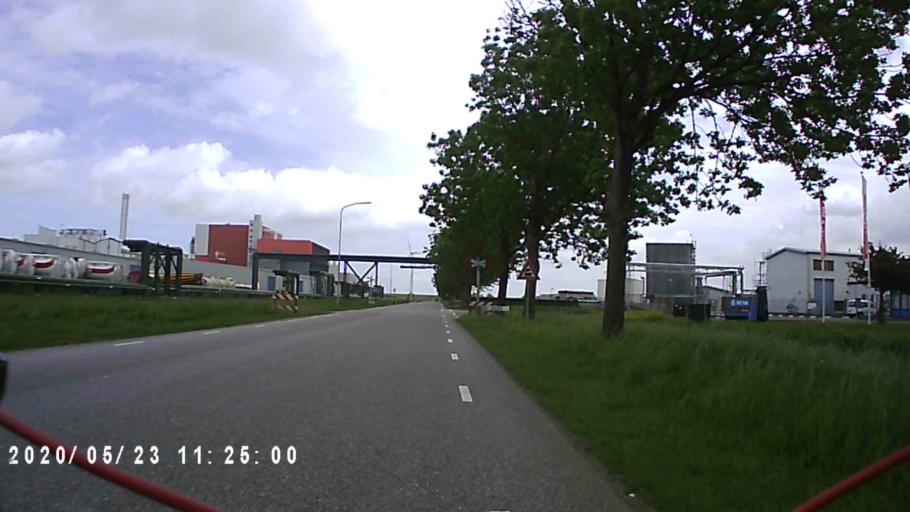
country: NL
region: Groningen
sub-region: Gemeente Delfzijl
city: Delfzijl
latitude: 53.3057
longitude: 6.9882
